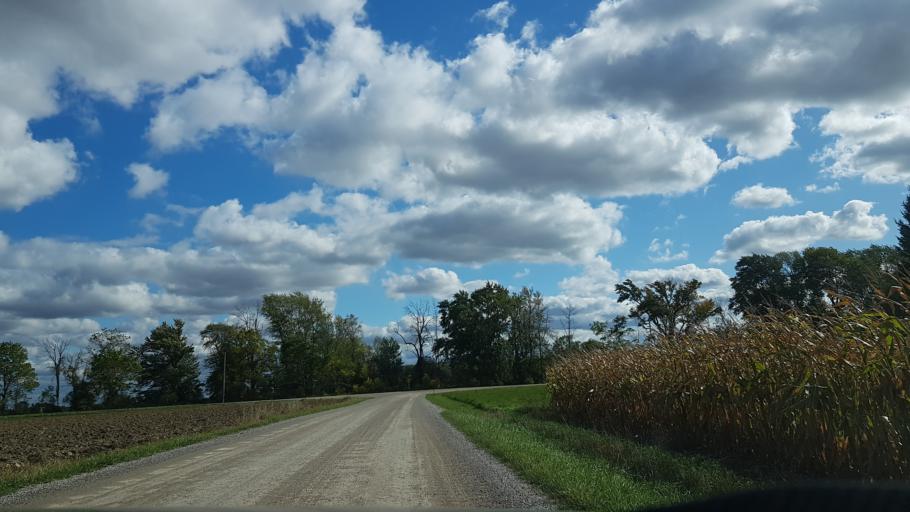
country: CA
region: Ontario
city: Lambton Shores
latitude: 43.2202
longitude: -81.8077
